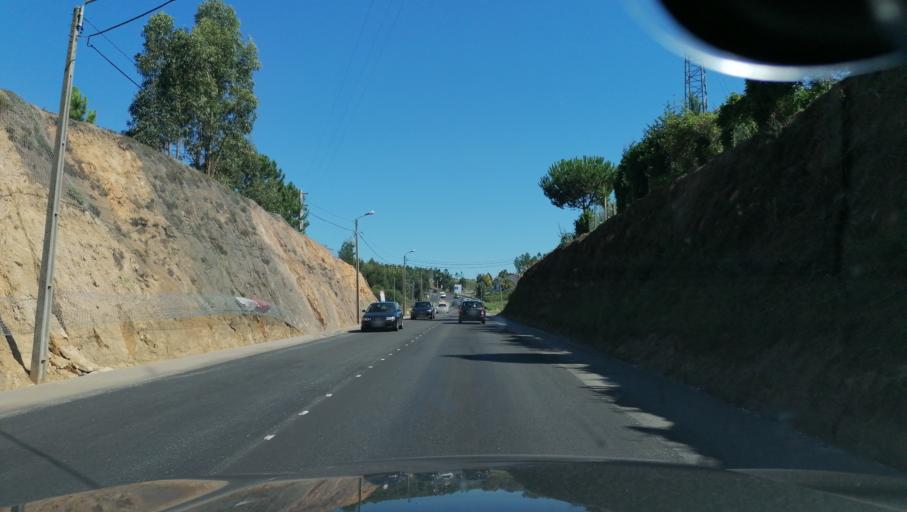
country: PT
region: Aveiro
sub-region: Santa Maria da Feira
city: Arrifana
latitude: 40.9278
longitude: -8.5096
